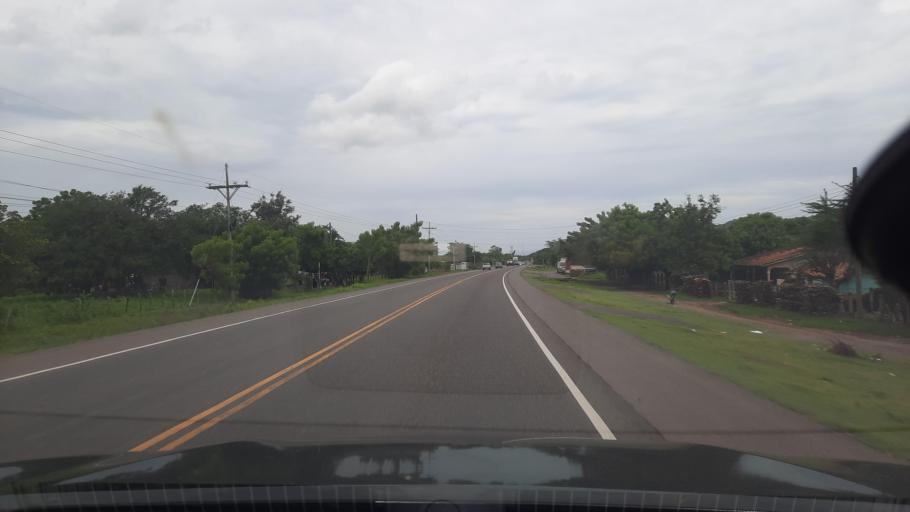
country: HN
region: Valle
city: Jicaro Galan
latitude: 13.5130
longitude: -87.4398
